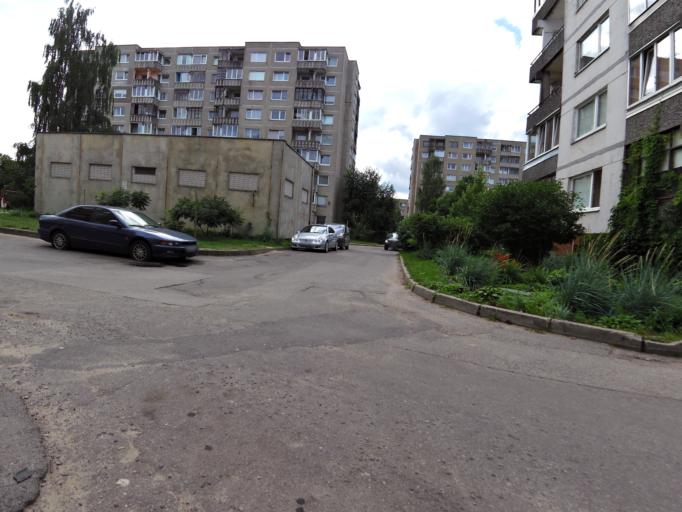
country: LT
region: Vilnius County
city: Seskine
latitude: 54.7162
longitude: 25.2412
